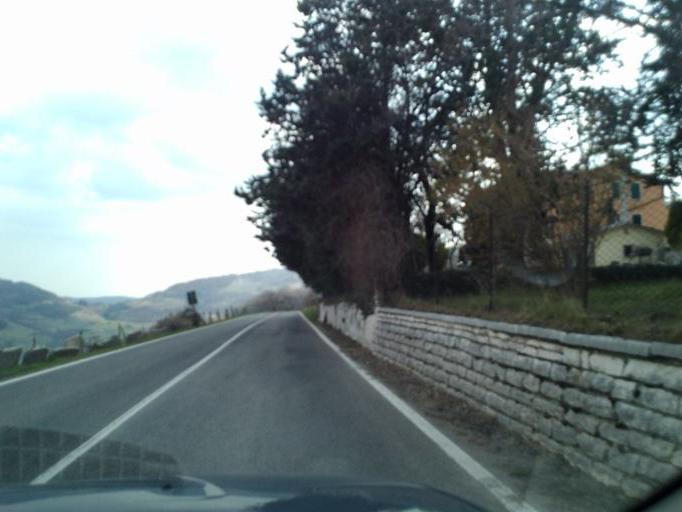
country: IT
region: Veneto
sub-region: Provincia di Verona
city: Sant'Anna d'Alfaedo
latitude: 45.6178
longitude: 10.9490
